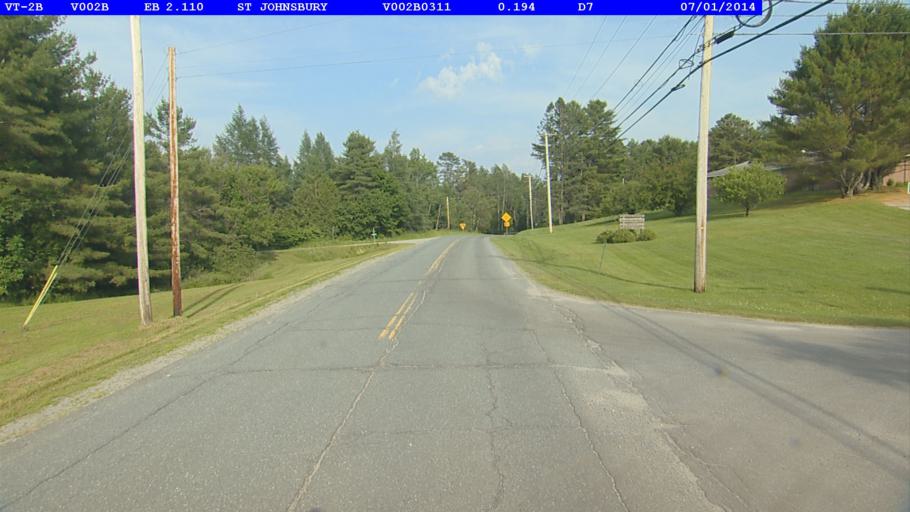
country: US
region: Vermont
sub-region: Caledonia County
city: St Johnsbury
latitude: 44.4284
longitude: -72.0524
